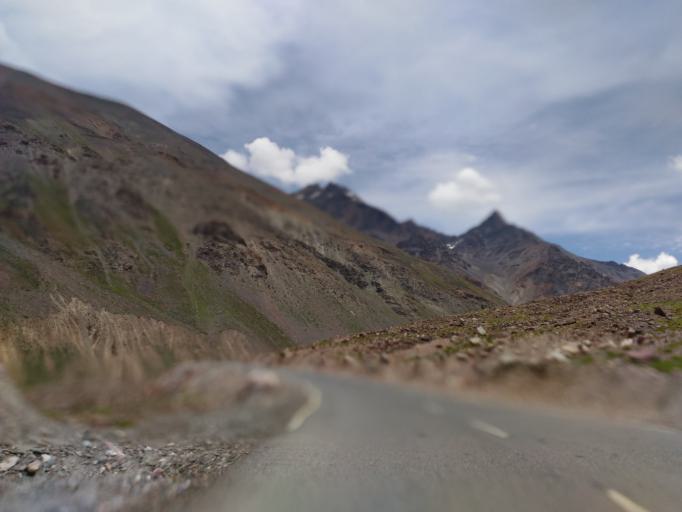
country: IN
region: Himachal Pradesh
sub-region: Lahul and Spiti
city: Kyelang
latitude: 32.7903
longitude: 77.2961
